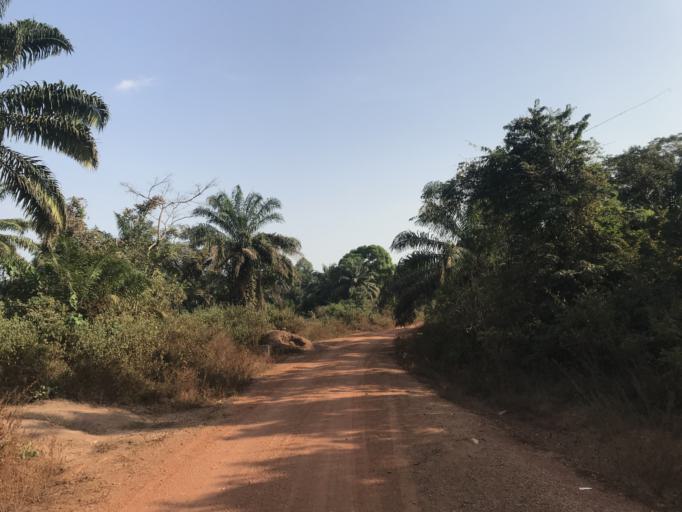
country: NG
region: Osun
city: Inisa
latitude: 7.7819
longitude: 4.3023
